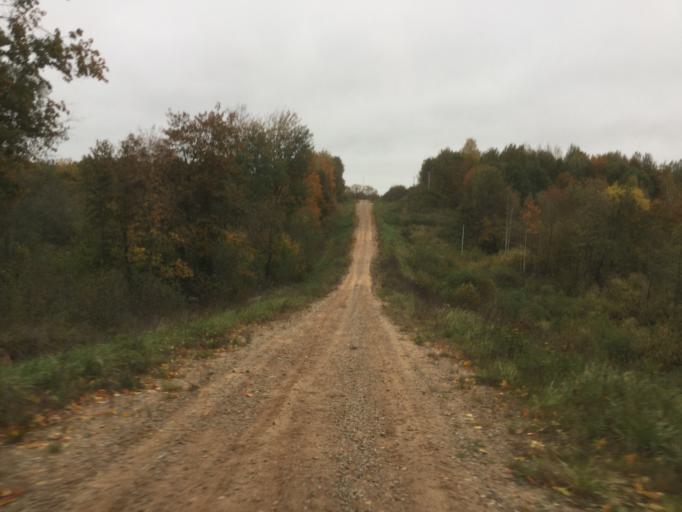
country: BY
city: Novolukoml'
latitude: 54.7337
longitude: 29.1356
